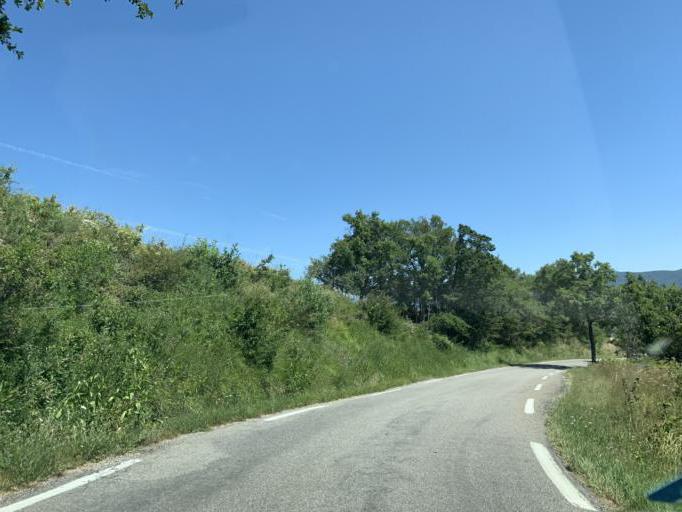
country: FR
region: Provence-Alpes-Cote d'Azur
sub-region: Departement des Hautes-Alpes
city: La Batie-Neuve
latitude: 44.5836
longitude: 6.1680
